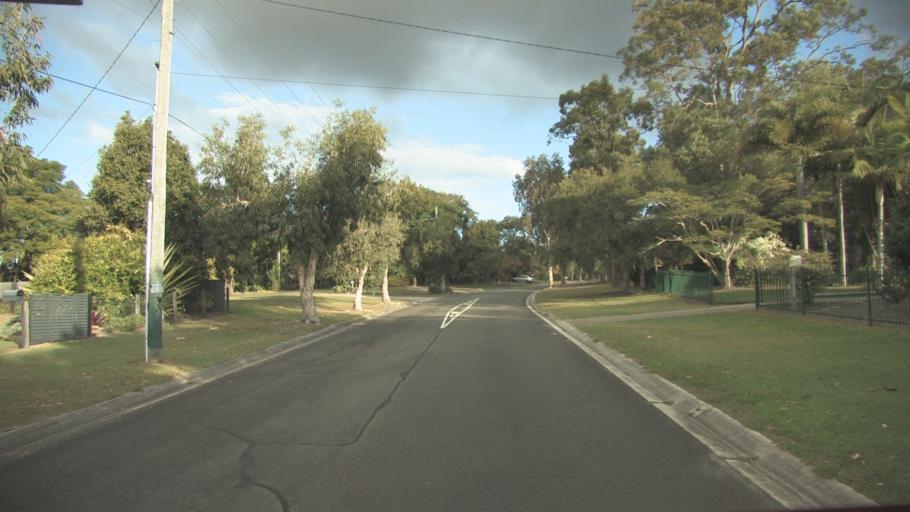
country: AU
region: Queensland
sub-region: Logan
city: Park Ridge South
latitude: -27.7037
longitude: 153.0207
